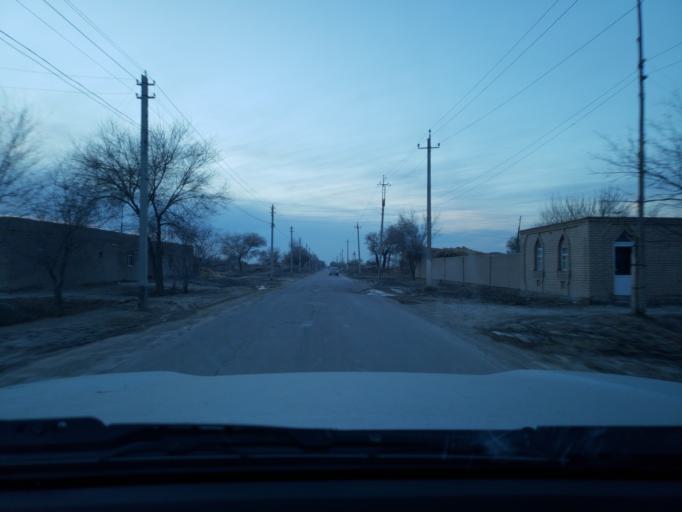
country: TM
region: Dasoguz
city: Tagta
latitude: 41.5833
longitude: 60.0670
